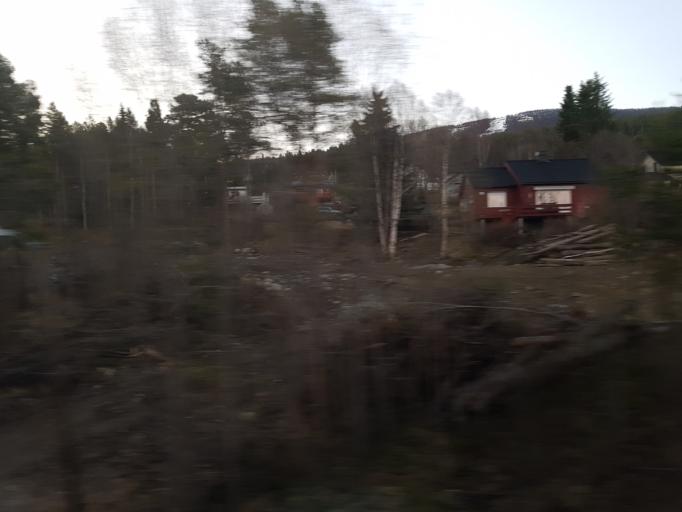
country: NO
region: Oppland
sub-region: Dovre
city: Dombas
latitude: 62.0766
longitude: 9.1339
